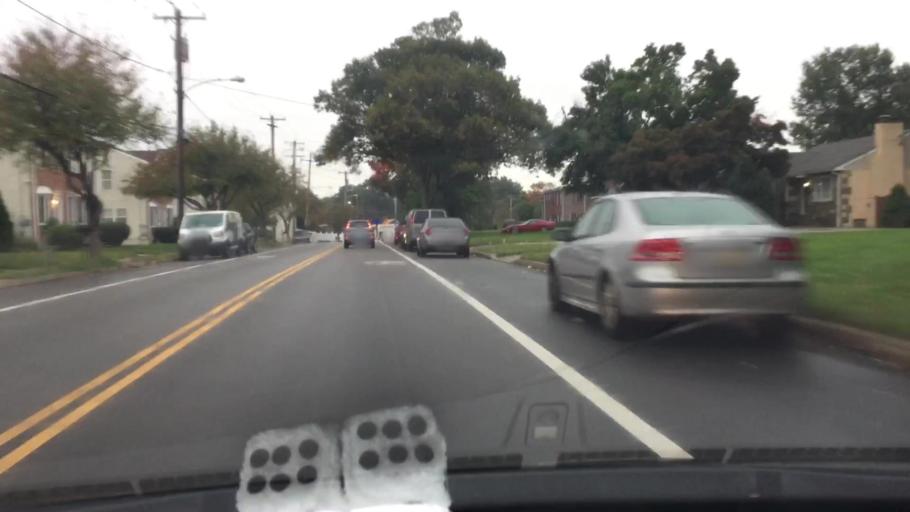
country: US
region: New Jersey
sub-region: Burlington County
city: Riverton
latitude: 40.0647
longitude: -75.0238
